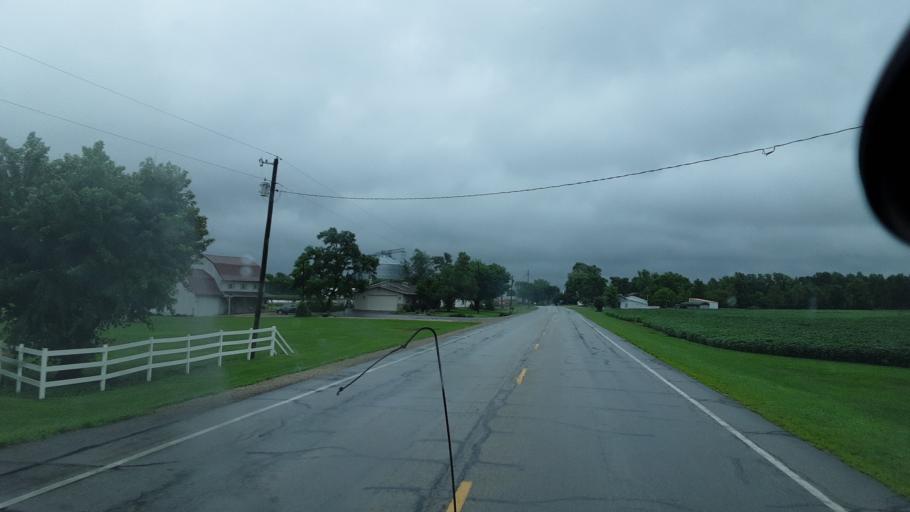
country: US
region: Indiana
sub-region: Adams County
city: Decatur
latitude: 40.7546
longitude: -84.8046
